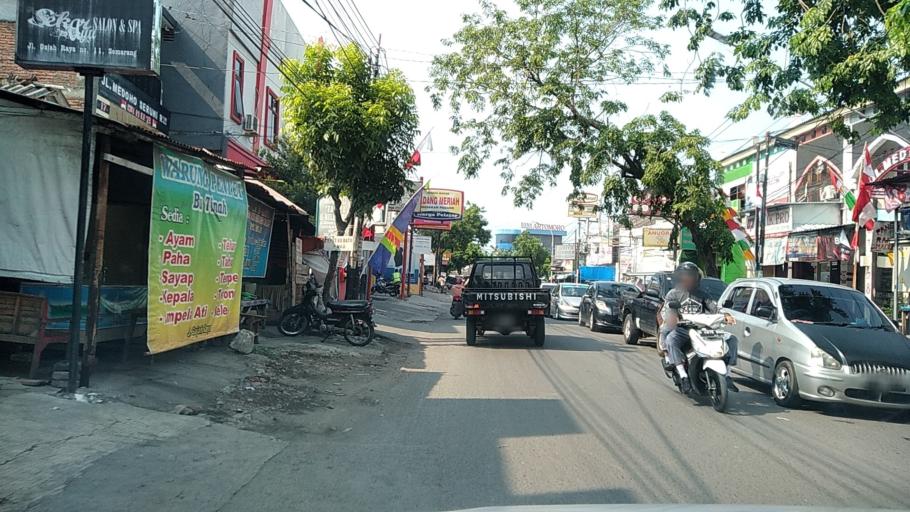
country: ID
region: Central Java
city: Semarang
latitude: -6.9889
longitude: 110.4480
